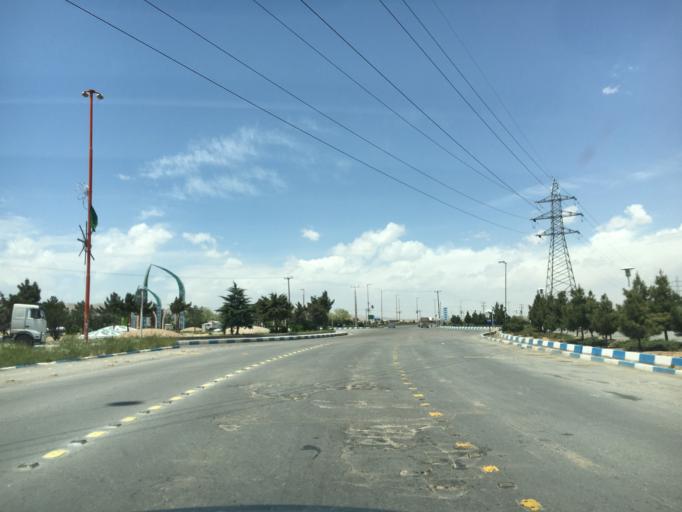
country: IR
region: Isfahan
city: Kashan
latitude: 33.4520
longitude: 51.1733
